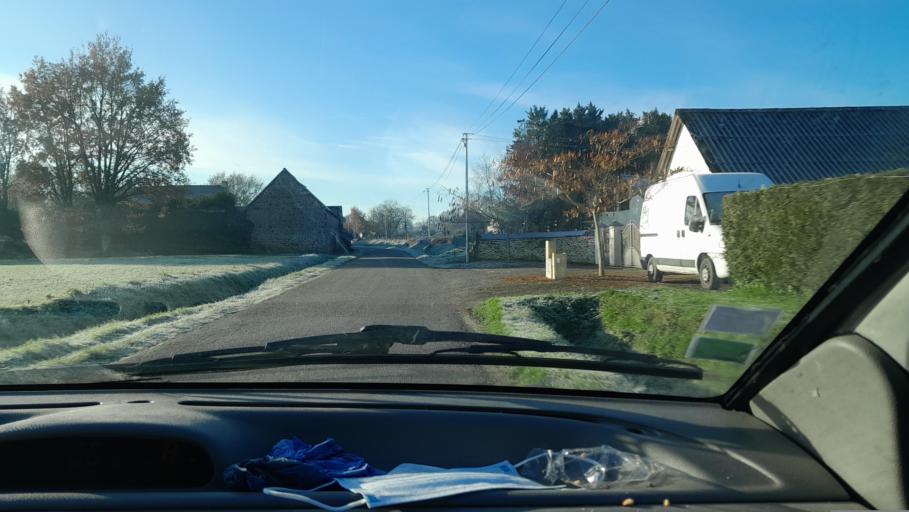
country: FR
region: Brittany
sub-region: Departement d'Ille-et-Vilaine
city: Rannee
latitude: 47.8792
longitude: -1.1828
